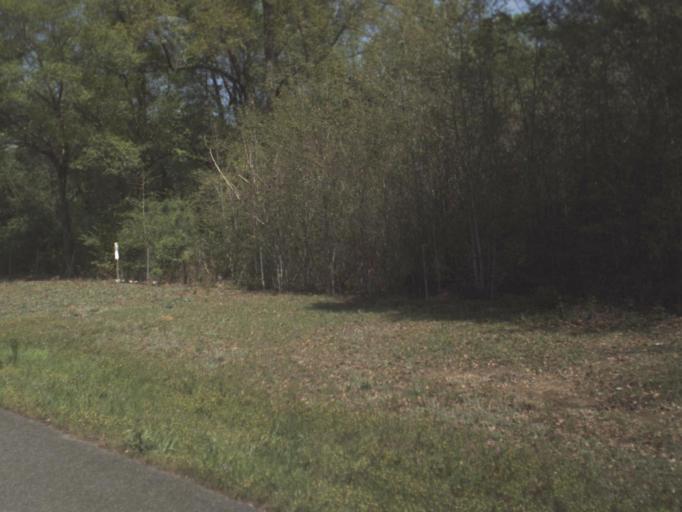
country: US
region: Florida
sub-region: Santa Rosa County
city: Point Baker
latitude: 30.8933
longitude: -86.9832
